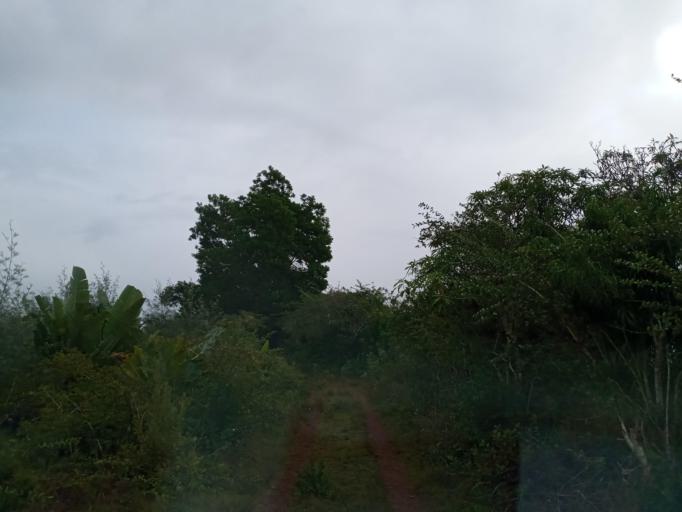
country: MG
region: Atsimo-Atsinanana
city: Vohipaho
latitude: -24.0084
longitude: 47.4128
